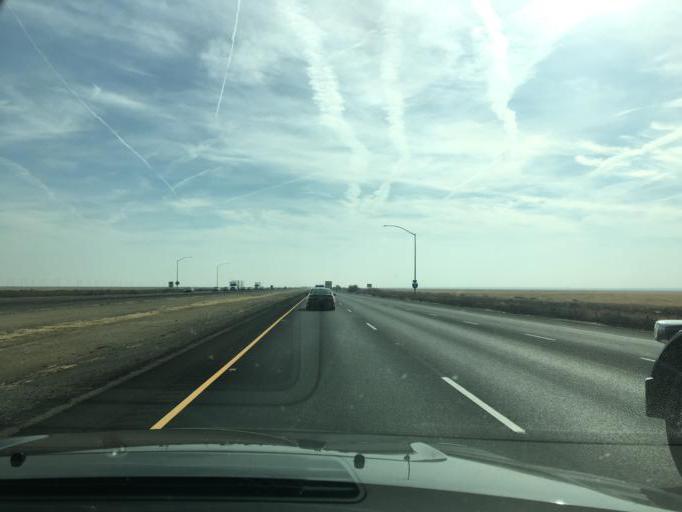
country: US
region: California
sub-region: Kern County
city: Lost Hills
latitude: 35.7305
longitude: -119.7384
